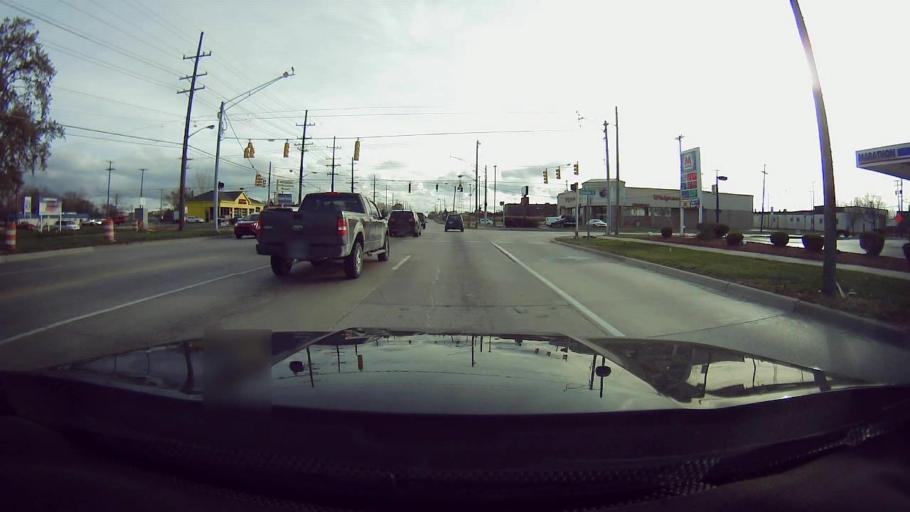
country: US
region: Michigan
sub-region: Macomb County
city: Eastpointe
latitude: 42.4784
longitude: -82.9846
